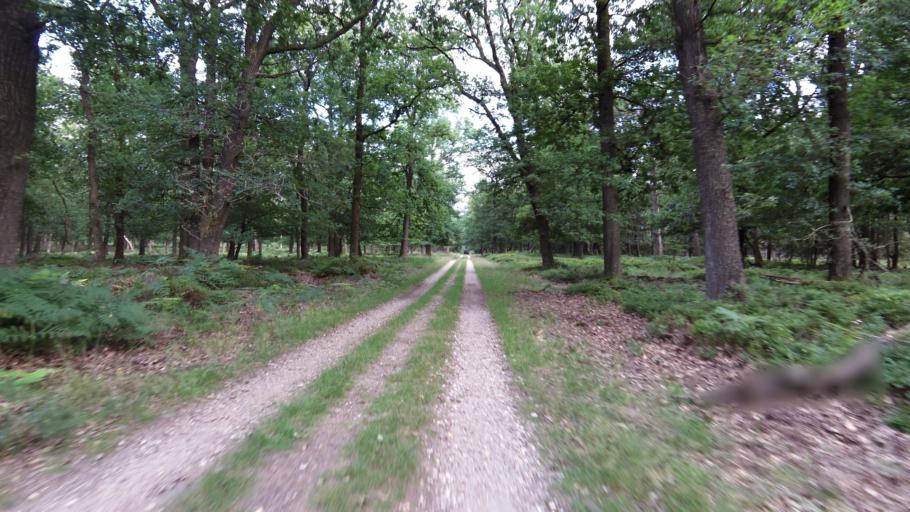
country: NL
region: Gelderland
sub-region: Gemeente Apeldoorn
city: Uddel
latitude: 52.2412
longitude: 5.8673
